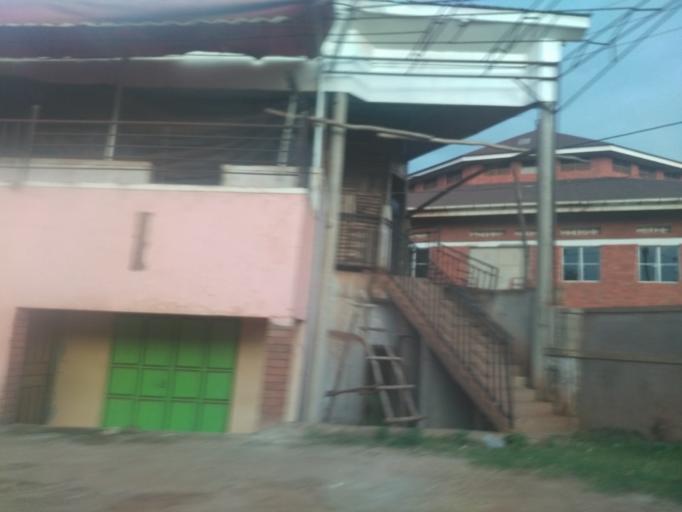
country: UG
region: Central Region
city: Kampala Central Division
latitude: 0.3806
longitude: 32.5648
